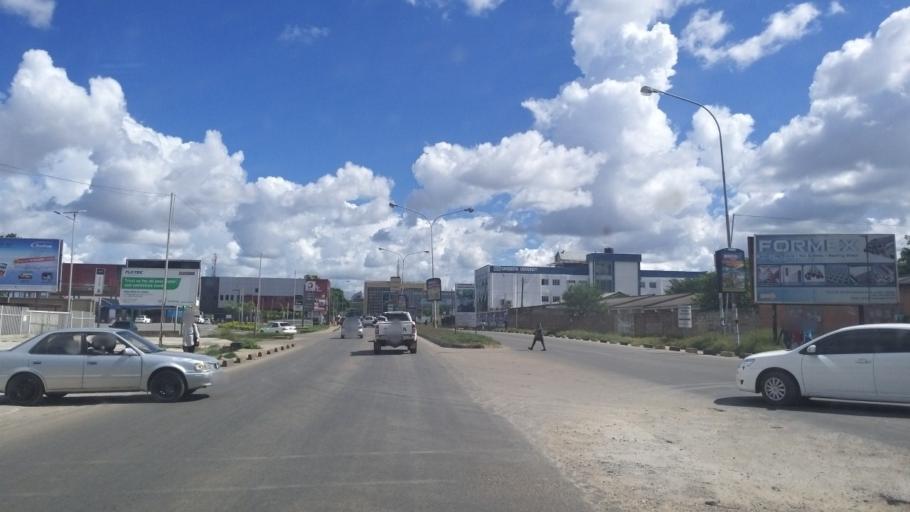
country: ZM
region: Lusaka
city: Lusaka
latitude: -15.4019
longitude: 28.2788
